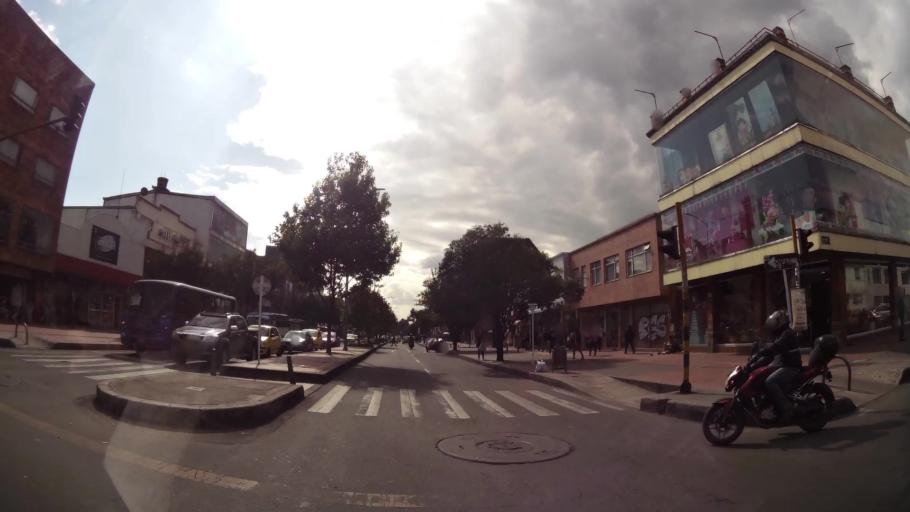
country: CO
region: Bogota D.C.
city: Bogota
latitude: 4.6411
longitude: -74.0699
